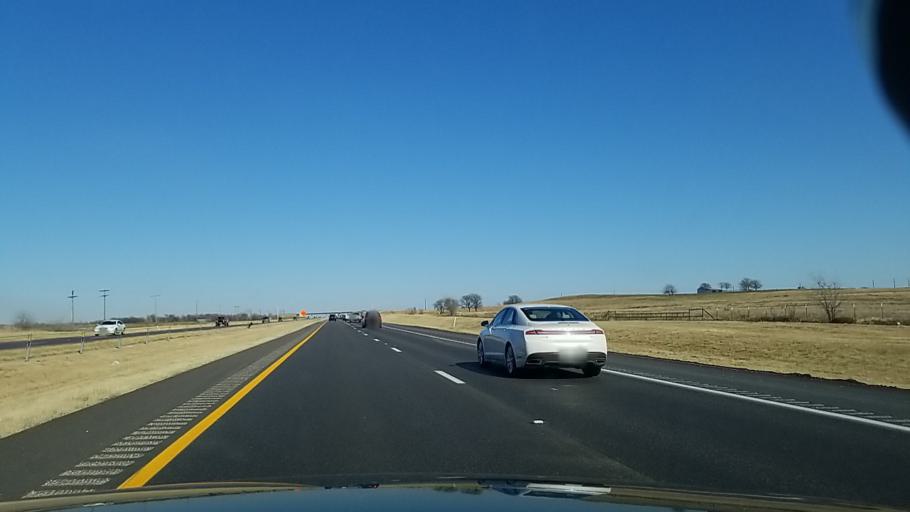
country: US
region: Texas
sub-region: Denton County
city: Justin
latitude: 33.0715
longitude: -97.2399
